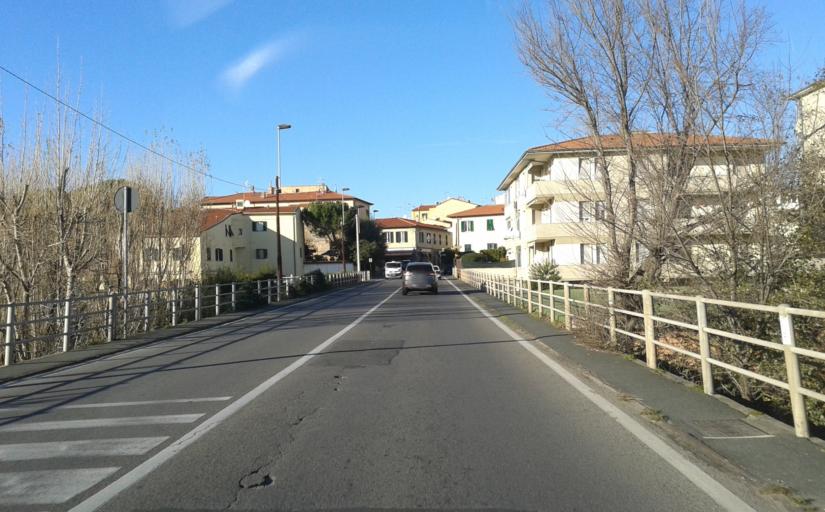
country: IT
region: Tuscany
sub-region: Provincia di Livorno
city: Livorno
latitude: 43.5145
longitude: 10.3257
